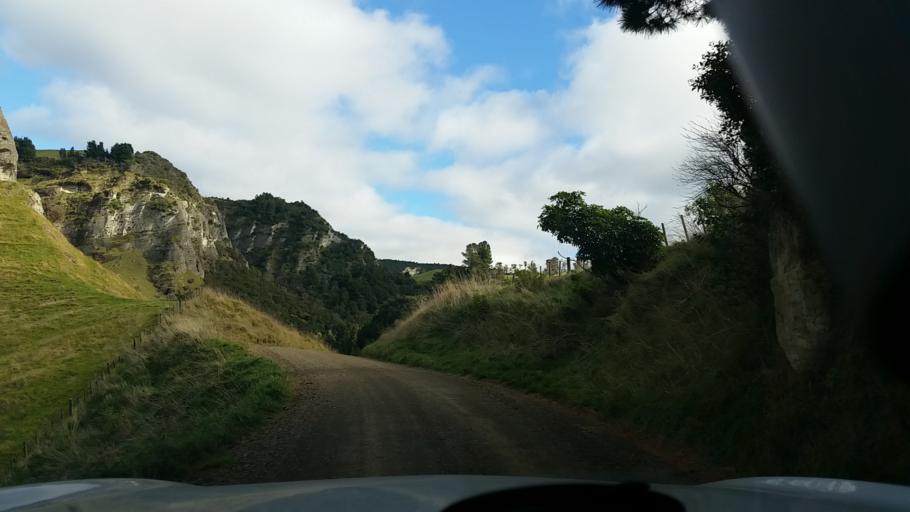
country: NZ
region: Hawke's Bay
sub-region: Napier City
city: Napier
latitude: -39.0952
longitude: 176.8694
